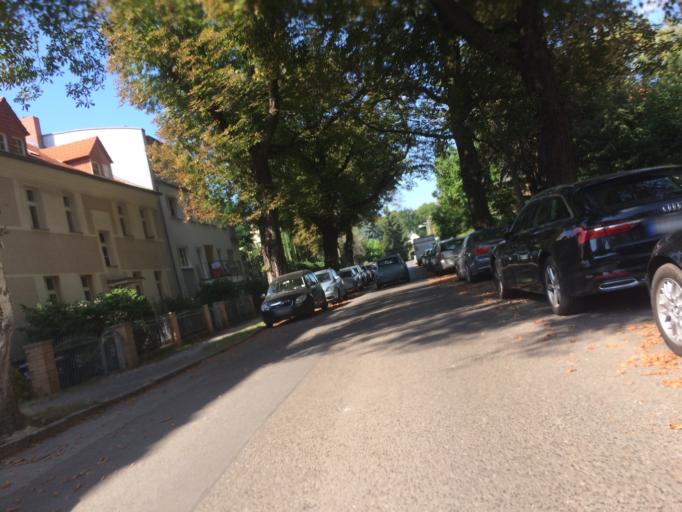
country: DE
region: Berlin
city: Niederschonhausen
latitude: 52.5924
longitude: 13.4122
